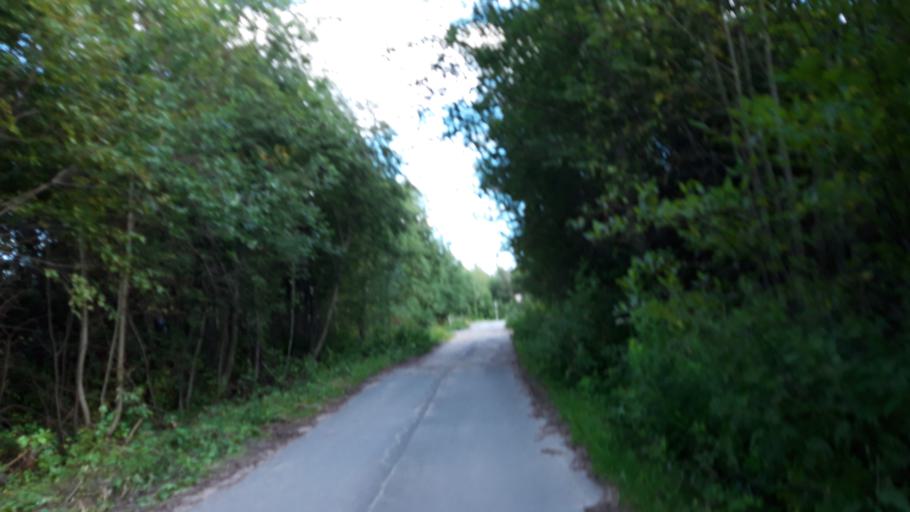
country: RU
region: Tverskaya
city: Konakovo
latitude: 56.6721
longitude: 36.7306
